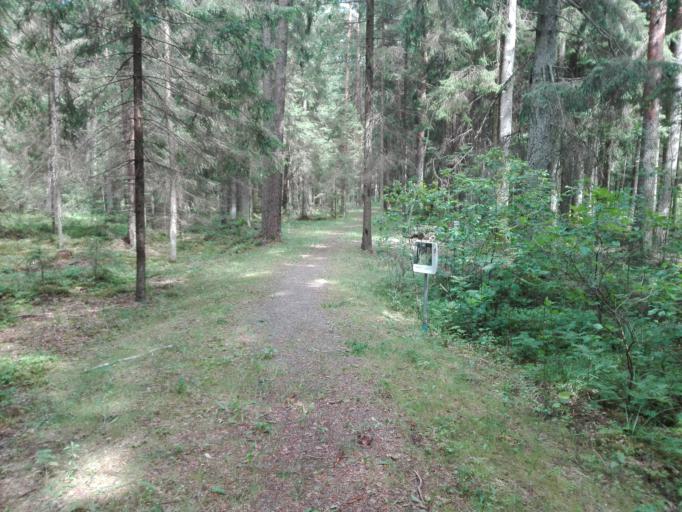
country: LT
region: Panevezys
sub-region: Birzai
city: Birzai
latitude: 56.2679
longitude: 24.7539
